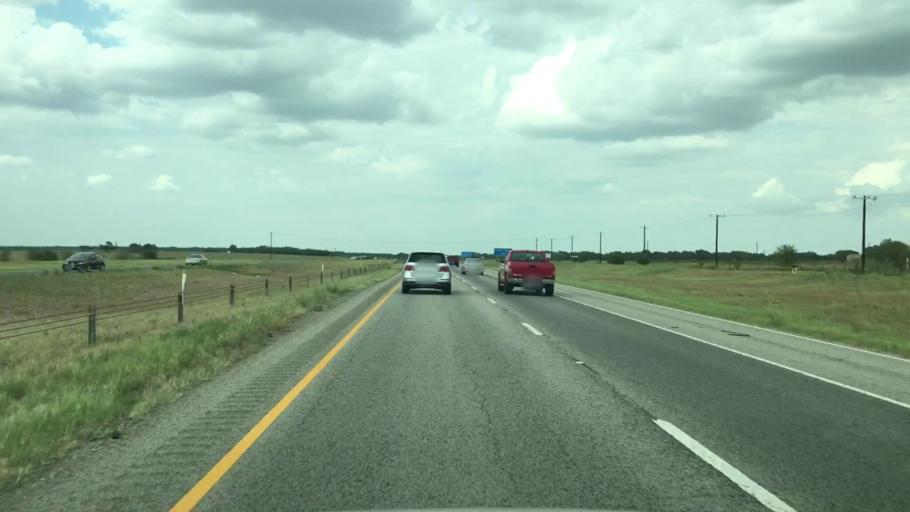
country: US
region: Texas
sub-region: Atascosa County
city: Pleasanton
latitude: 29.0131
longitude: -98.4310
